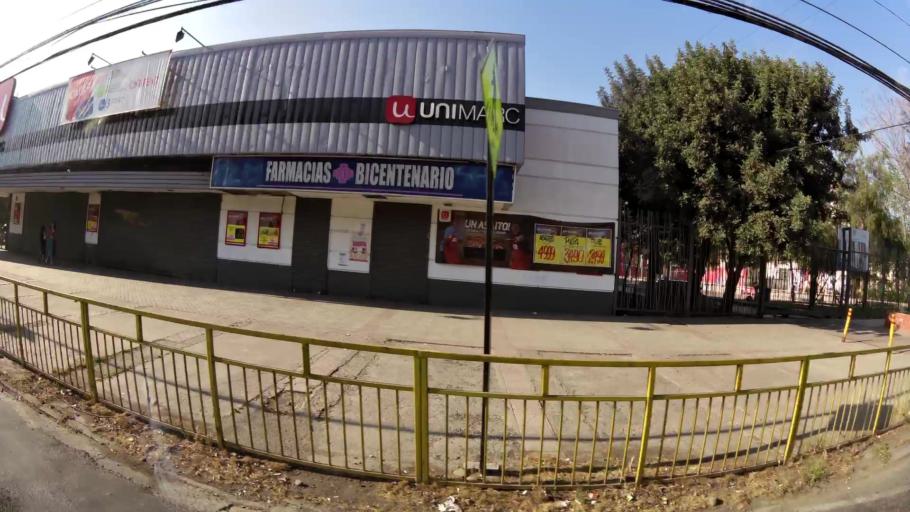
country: CL
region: Santiago Metropolitan
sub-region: Provincia de Santiago
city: Santiago
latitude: -33.4197
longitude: -70.6704
